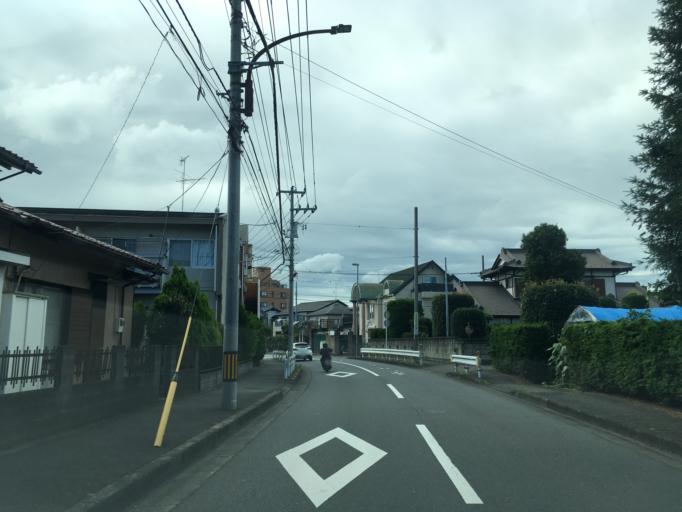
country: JP
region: Tokyo
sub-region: Machida-shi
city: Machida
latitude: 35.5602
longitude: 139.4093
